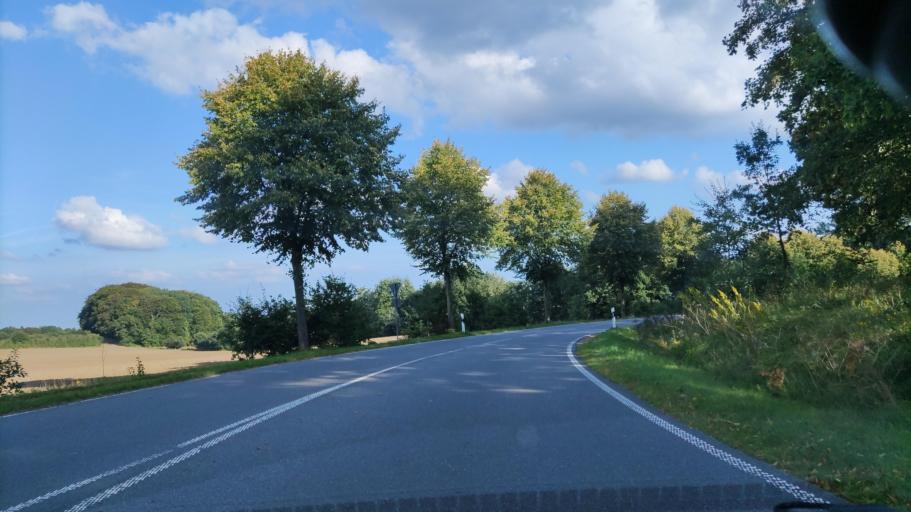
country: DE
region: Schleswig-Holstein
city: Aukrug
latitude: 54.0667
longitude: 9.7709
